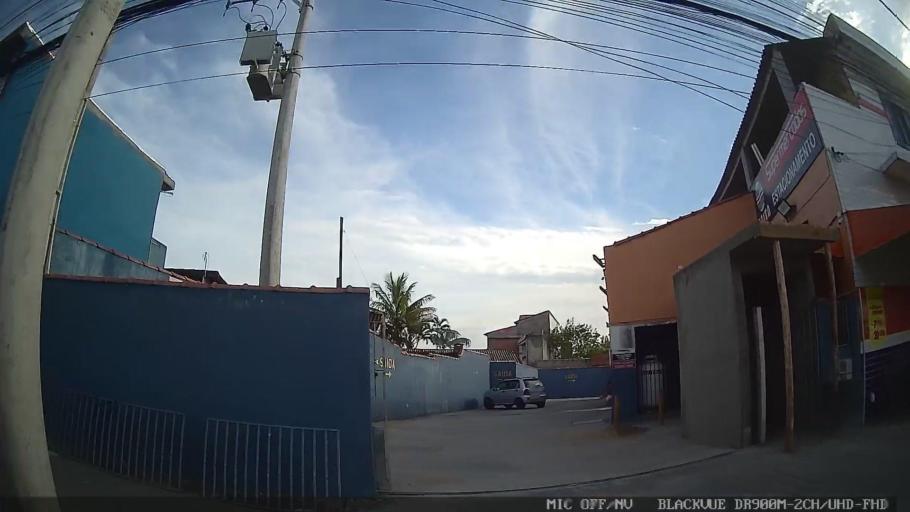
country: BR
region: Sao Paulo
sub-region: Itanhaem
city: Itanhaem
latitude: -24.1623
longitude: -46.7622
